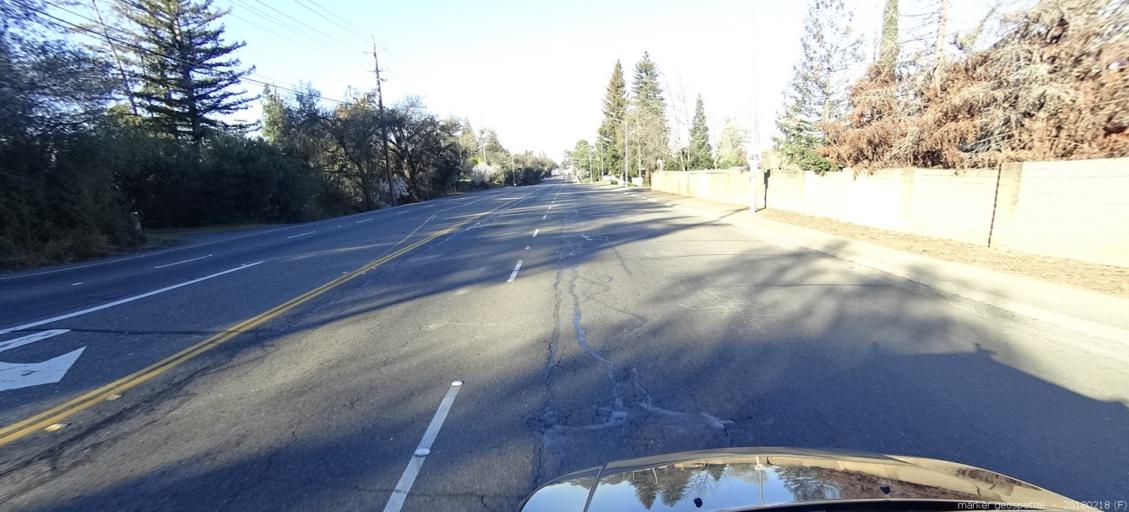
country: US
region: California
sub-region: Sacramento County
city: Orangevale
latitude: 38.6787
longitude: -121.2505
